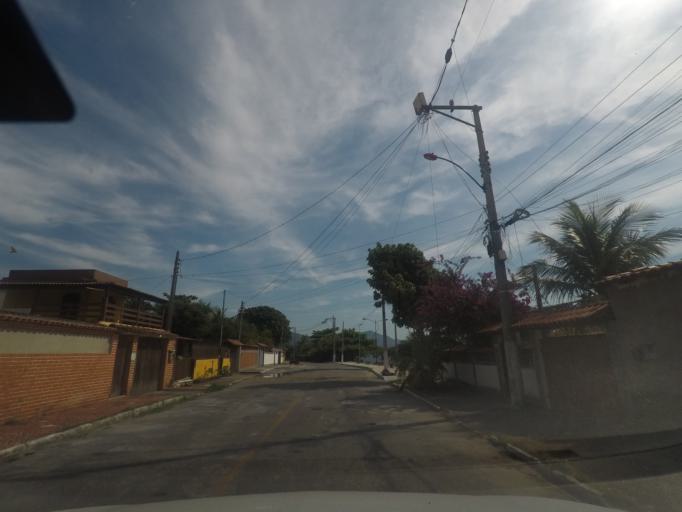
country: BR
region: Rio de Janeiro
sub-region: Marica
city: Marica
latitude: -22.9554
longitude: -42.8097
